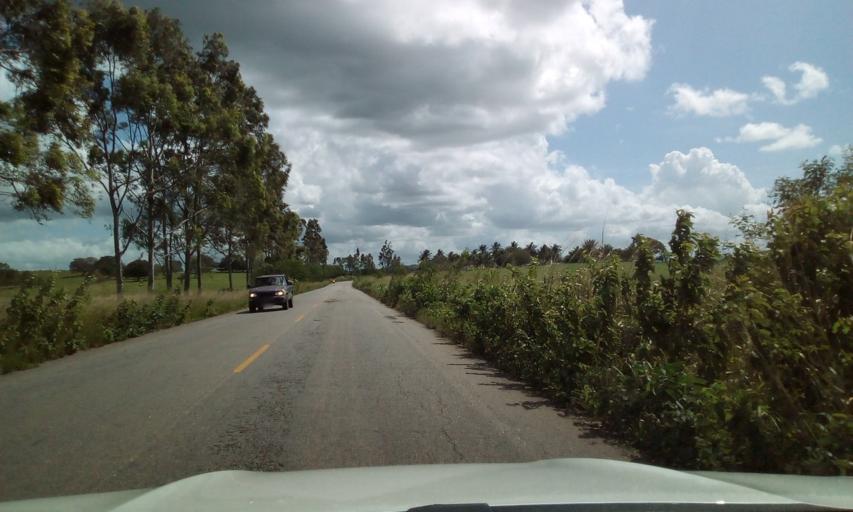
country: BR
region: Paraiba
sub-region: Guarabira
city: Guarabira
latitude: -6.8609
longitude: -35.4200
